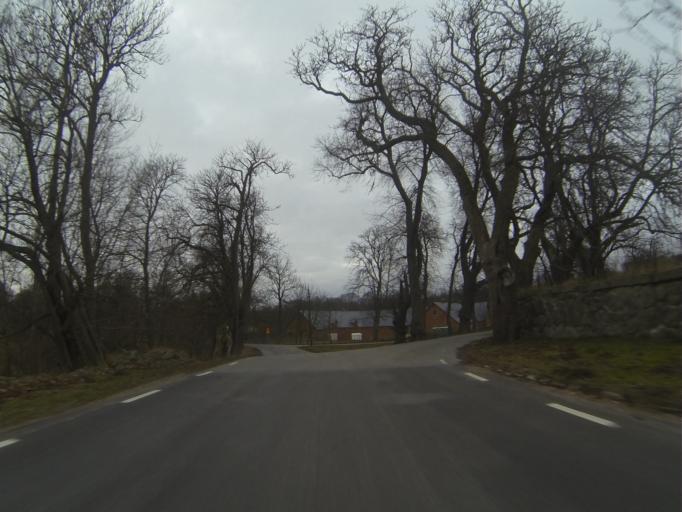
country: SE
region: Skane
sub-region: Lunds Kommun
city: Genarp
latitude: 55.5824
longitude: 13.4302
